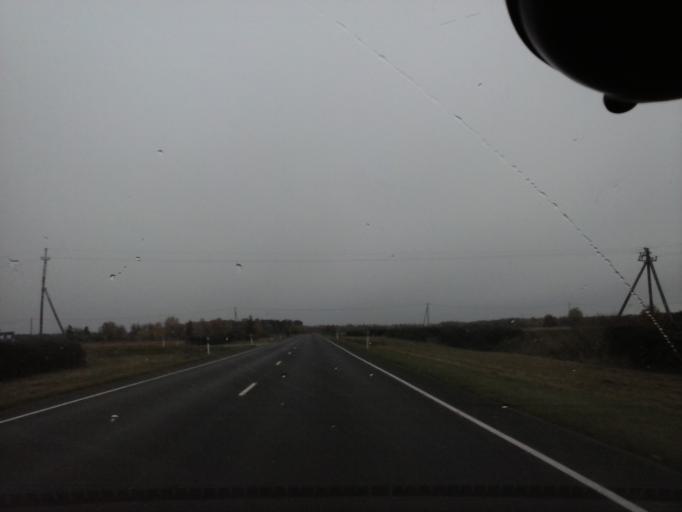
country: EE
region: Viljandimaa
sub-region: Vohma linn
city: Vohma
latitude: 58.7002
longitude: 25.6246
